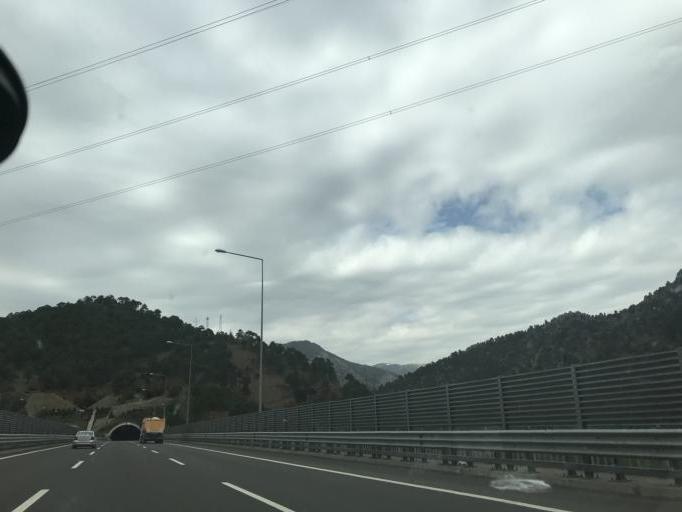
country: TR
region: Nigde
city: Ciftehan
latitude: 37.5060
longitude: 34.8210
